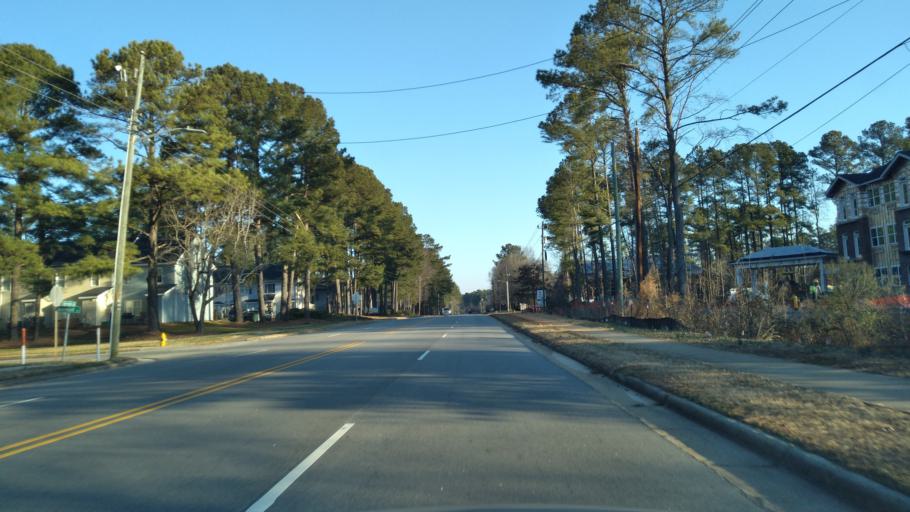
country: US
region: North Carolina
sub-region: Wake County
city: Garner
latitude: 35.6900
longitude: -78.6169
